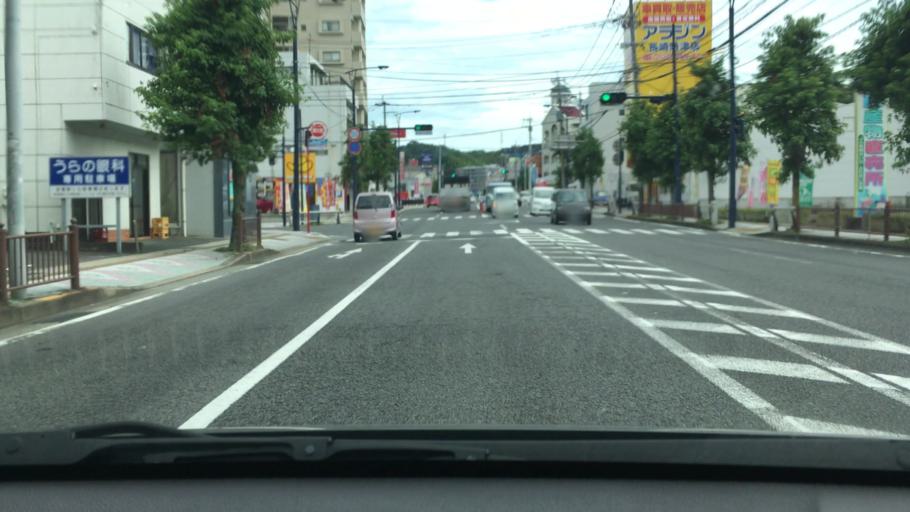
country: JP
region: Nagasaki
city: Togitsu
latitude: 32.8288
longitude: 129.8477
